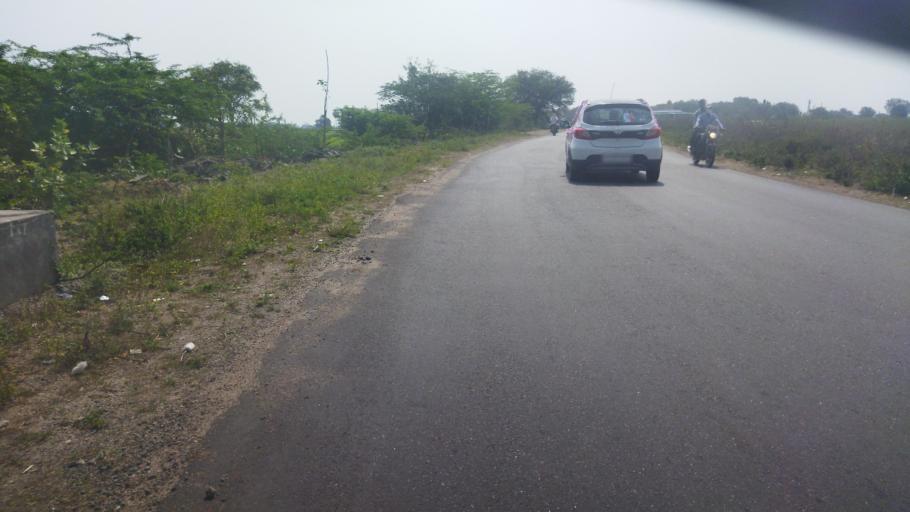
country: IN
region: Telangana
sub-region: Nalgonda
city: Nalgonda
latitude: 17.0987
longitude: 79.2855
